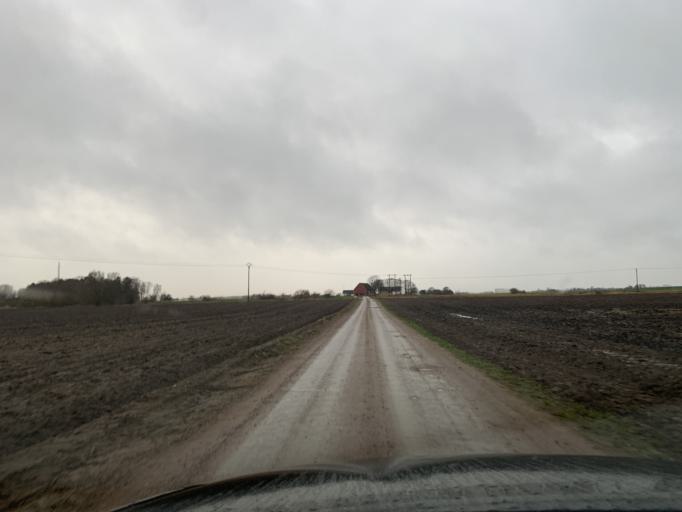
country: SE
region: Skane
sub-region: Kavlinge Kommun
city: Hofterup
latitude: 55.8399
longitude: 12.9962
